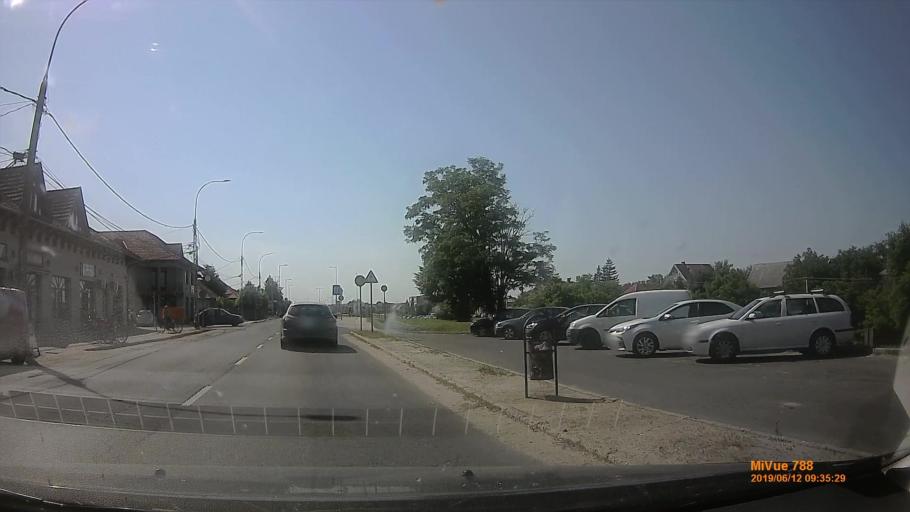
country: HU
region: Pest
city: Gyal
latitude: 47.3844
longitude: 19.2116
